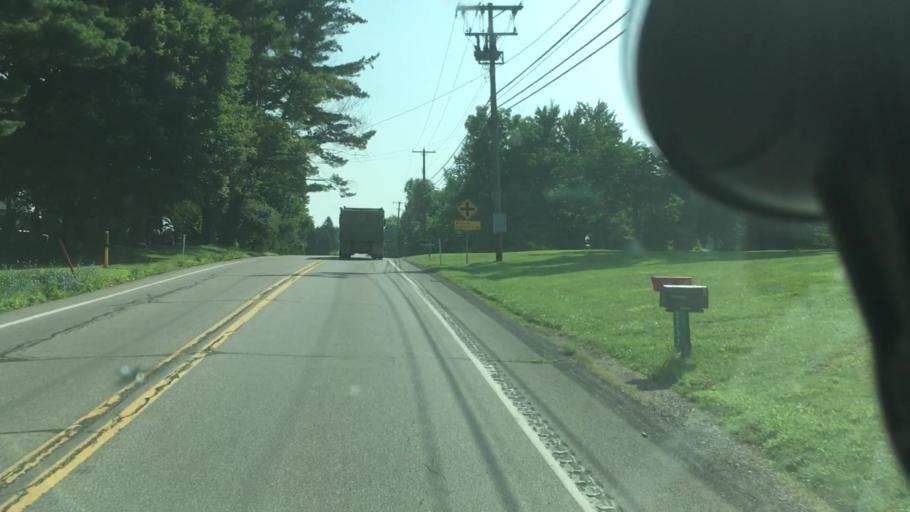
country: US
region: Pennsylvania
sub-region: Lawrence County
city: New Castle
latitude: 41.0150
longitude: -80.2212
